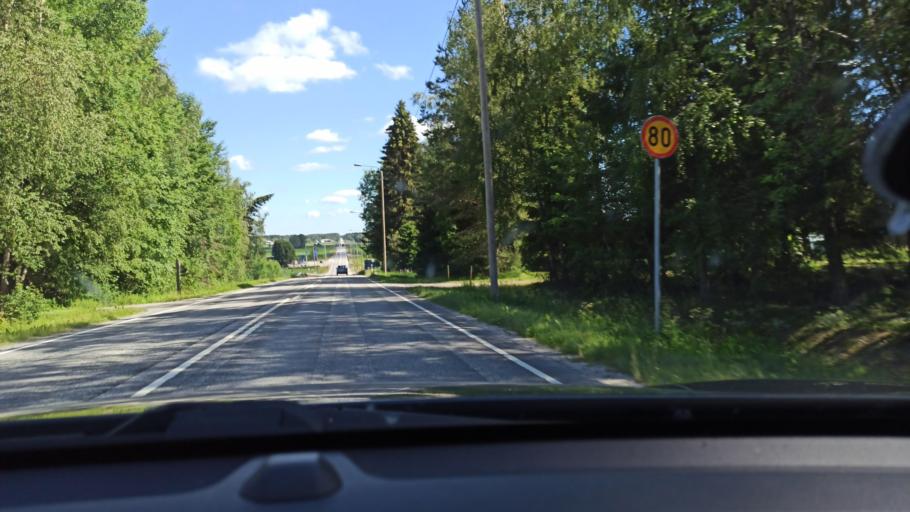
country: FI
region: Ostrobothnia
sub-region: Vaasa
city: Teeriniemi
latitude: 62.9989
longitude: 21.6665
